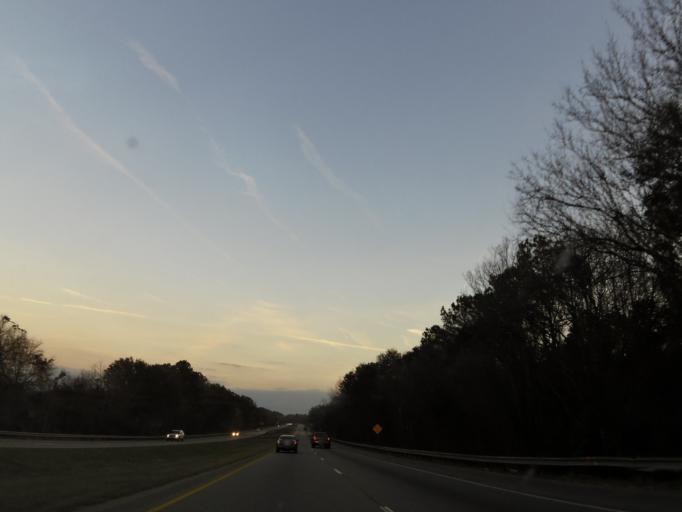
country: US
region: Georgia
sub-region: Dougherty County
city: Albany
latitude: 31.6019
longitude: -84.1480
